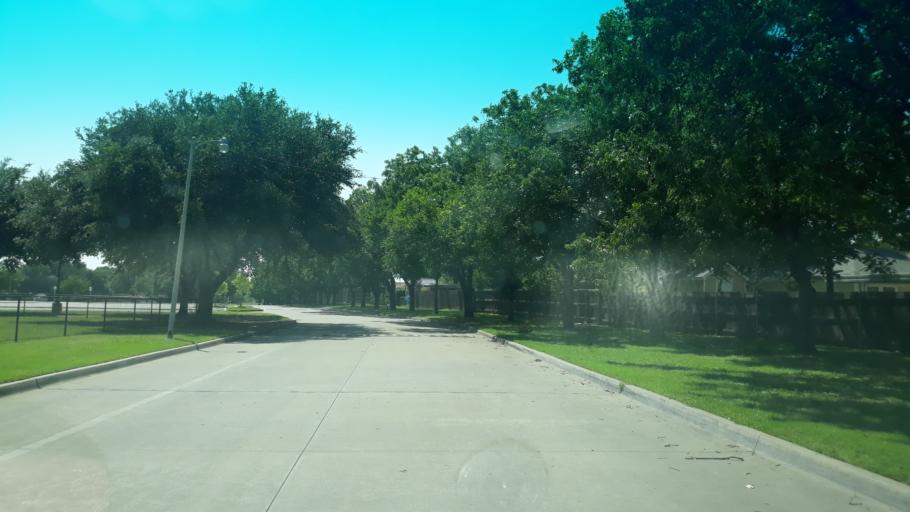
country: US
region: Texas
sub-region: Dallas County
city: Irving
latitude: 32.8551
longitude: -96.9560
